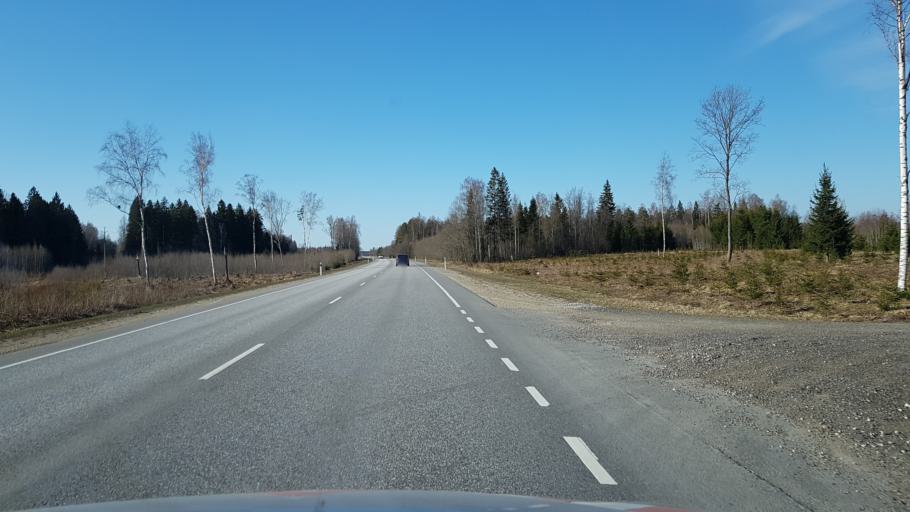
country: EE
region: Ida-Virumaa
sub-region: Johvi vald
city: Johvi
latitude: 59.2023
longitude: 27.3454
